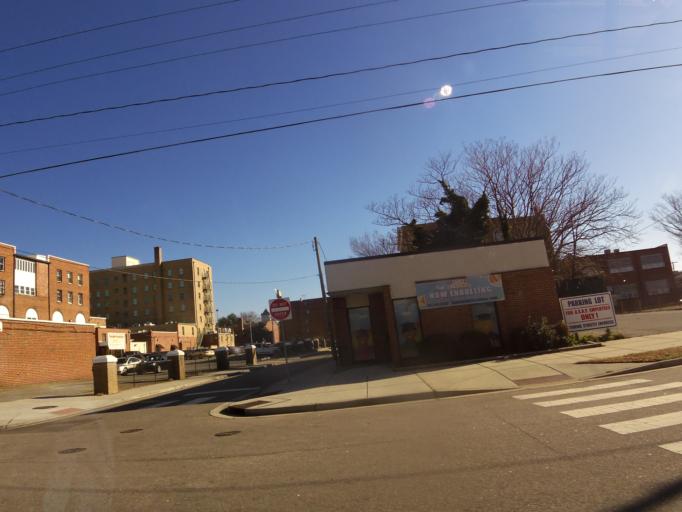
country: US
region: Virginia
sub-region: City of Portsmouth
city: Portsmouth
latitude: 36.8345
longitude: -76.3039
